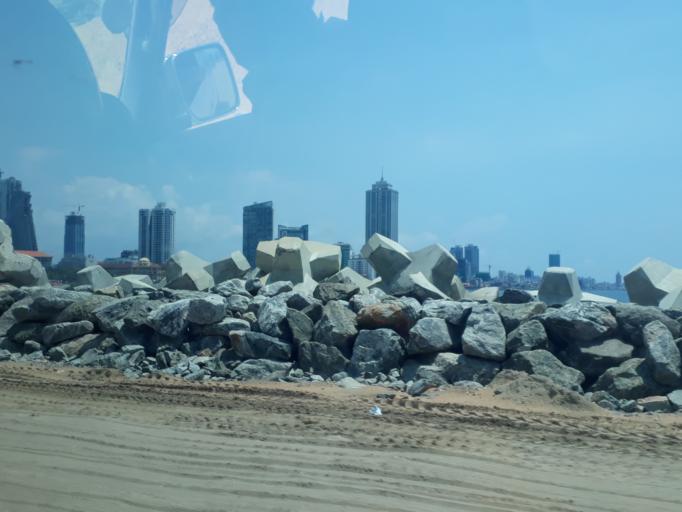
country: LK
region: Western
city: Colombo
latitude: 6.9251
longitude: 79.8396
